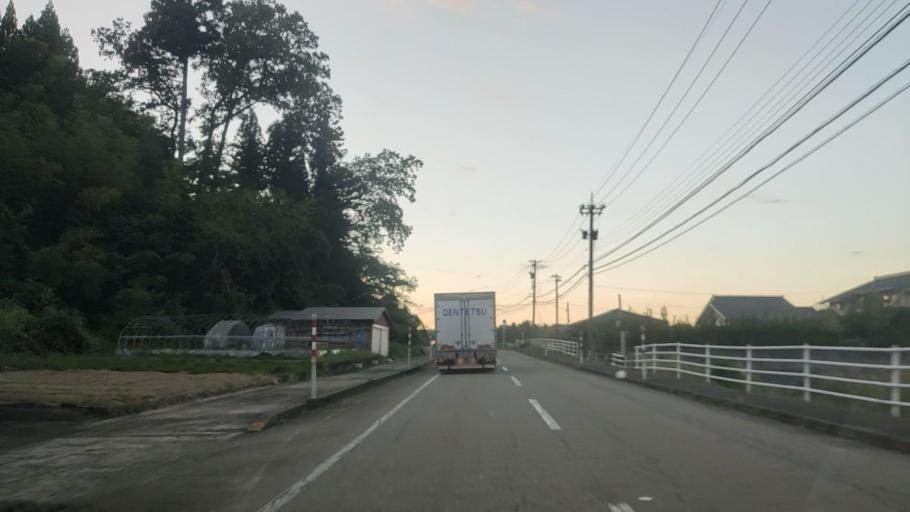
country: JP
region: Ishikawa
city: Tsubata
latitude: 36.6548
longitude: 136.7591
